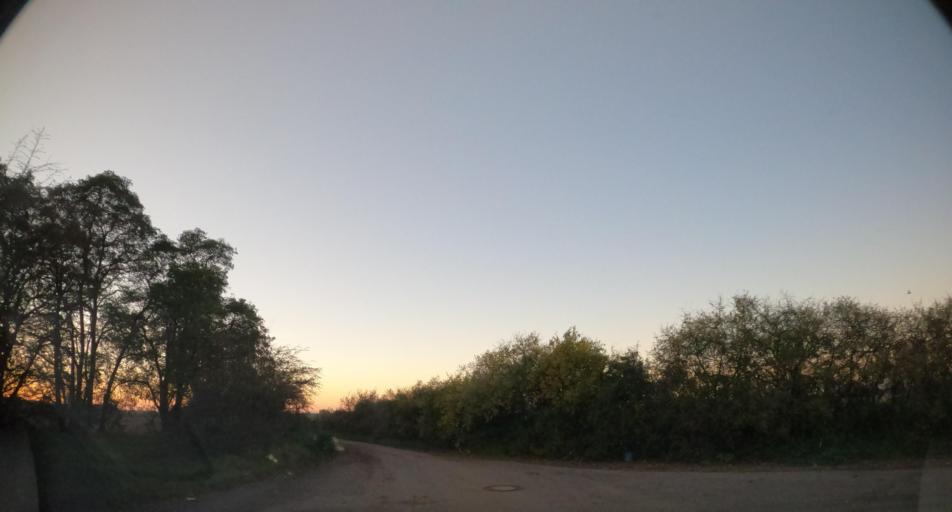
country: DE
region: Mecklenburg-Vorpommern
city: Ducherow
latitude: 53.7784
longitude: 13.8596
